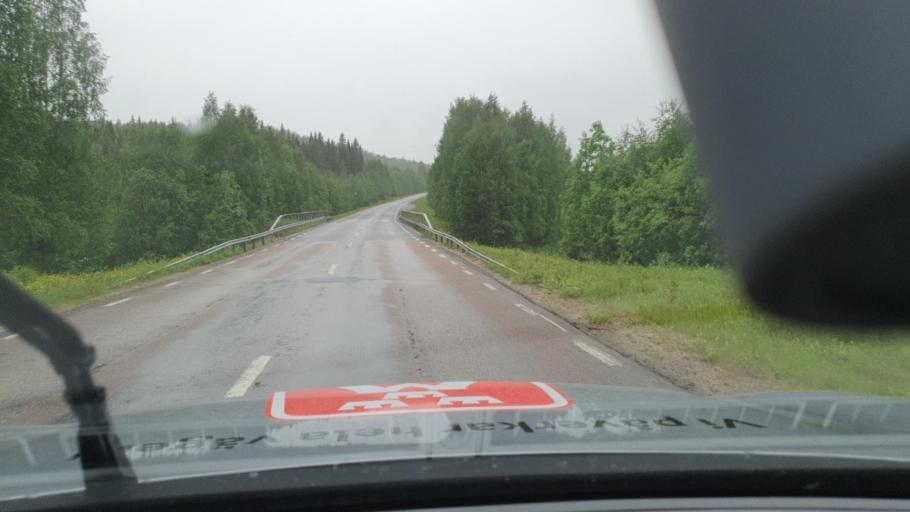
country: SE
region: Norrbotten
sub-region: Overtornea Kommun
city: OEvertornea
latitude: 66.4389
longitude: 23.3238
